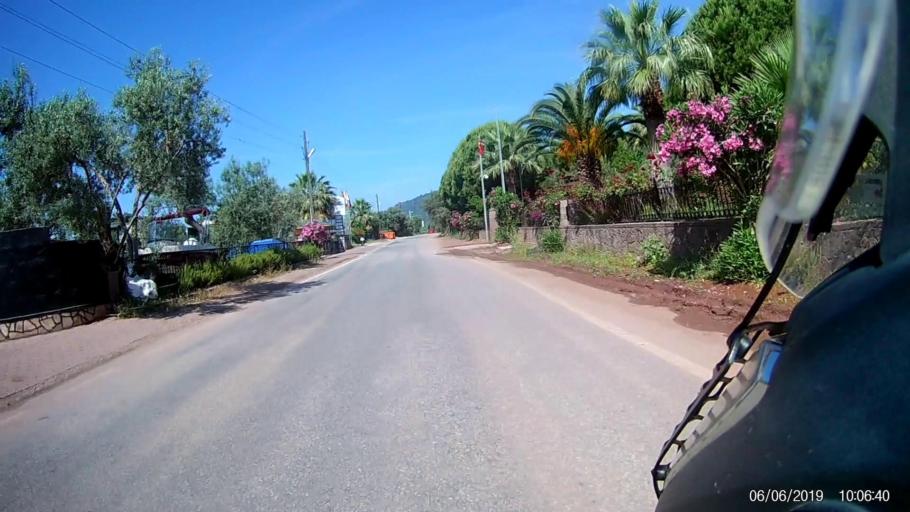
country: TR
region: Canakkale
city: Ayvacik
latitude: 39.5231
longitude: 26.4674
